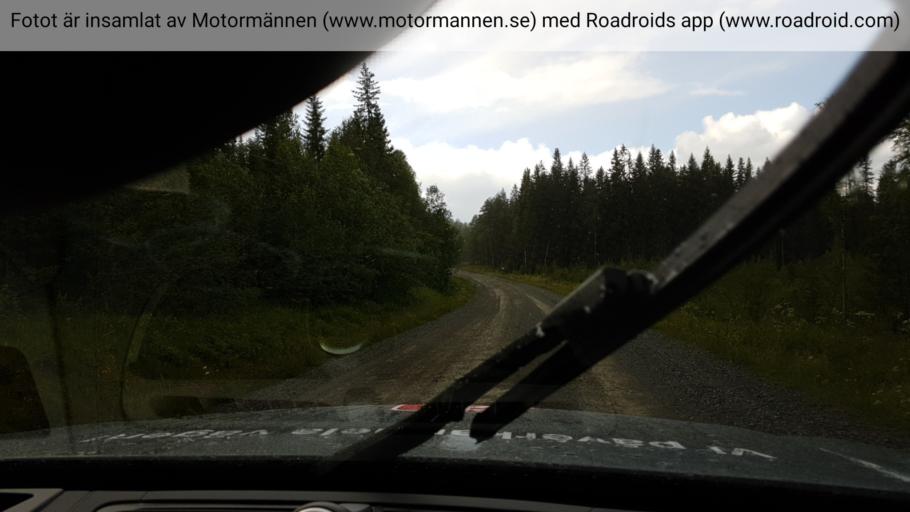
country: SE
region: Jaemtland
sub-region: Bergs Kommun
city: Hoverberg
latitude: 63.0007
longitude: 14.1414
